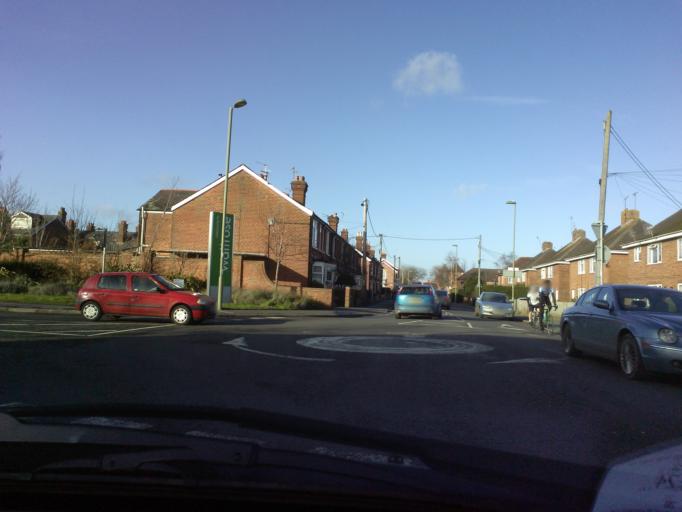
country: GB
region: England
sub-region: Hampshire
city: Romsey
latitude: 50.9907
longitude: -1.4937
